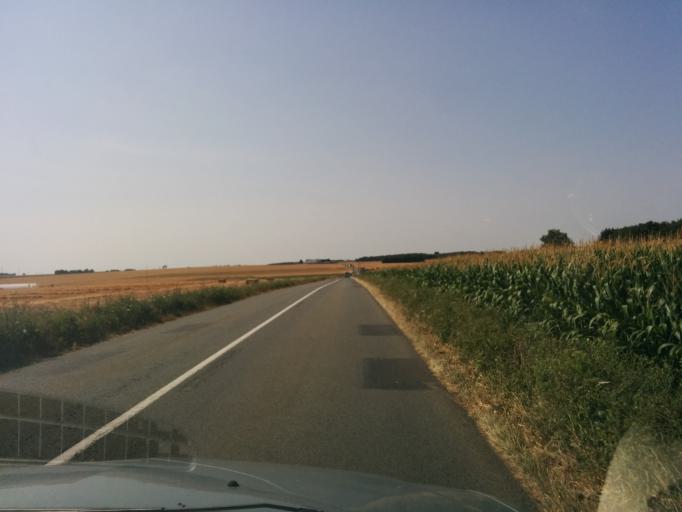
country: FR
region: Poitou-Charentes
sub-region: Departement de la Vienne
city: Mirebeau
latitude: 46.7296
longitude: 0.1960
